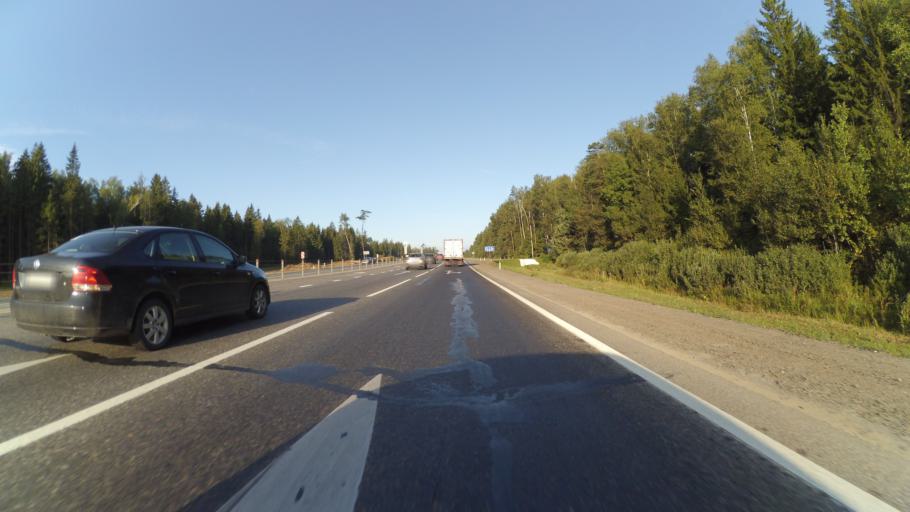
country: RU
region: Moskovskaya
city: Bol'shiye Vyazemy
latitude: 55.5876
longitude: 36.8602
